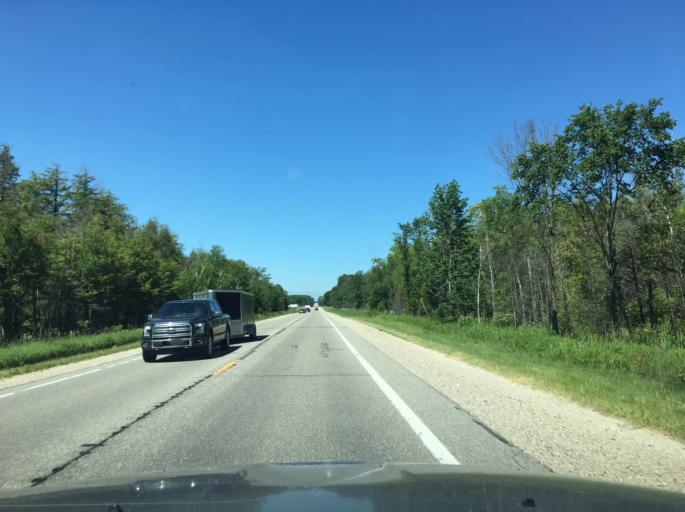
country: US
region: Michigan
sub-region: Osceola County
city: Reed City
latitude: 43.8728
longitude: -85.4101
